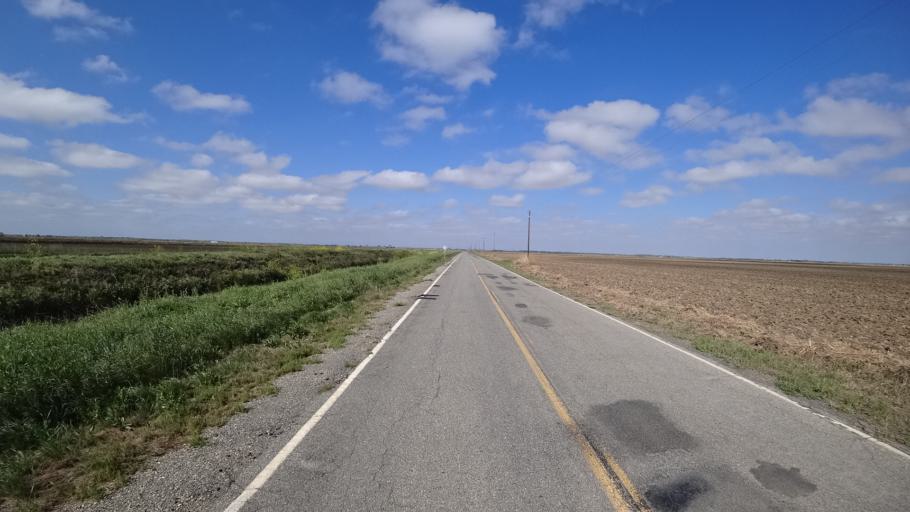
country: US
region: California
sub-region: Colusa County
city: Colusa
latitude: 39.3624
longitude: -121.9375
